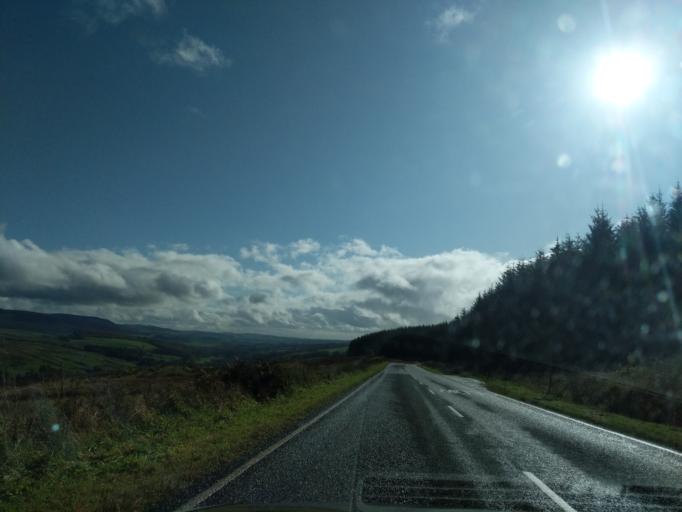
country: GB
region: Scotland
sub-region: Dumfries and Galloway
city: Moffat
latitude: 55.3746
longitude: -3.4769
